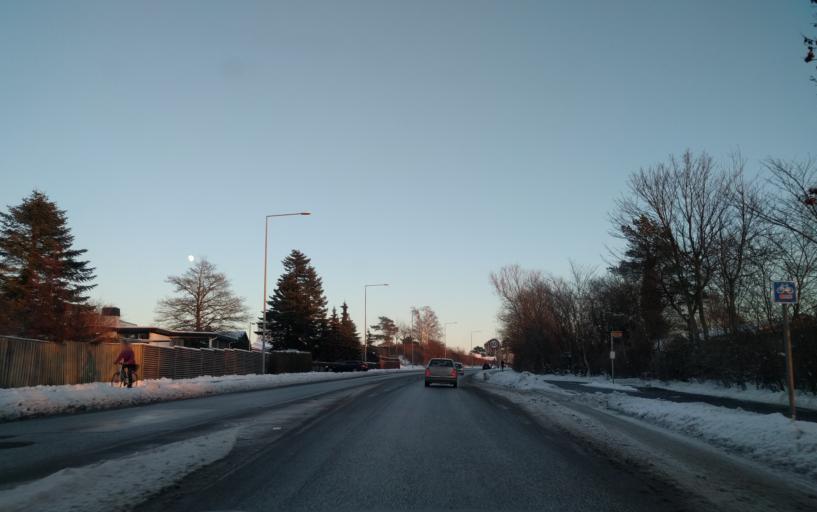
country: DK
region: North Denmark
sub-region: Alborg Kommune
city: Aalborg
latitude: 57.0263
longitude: 9.9340
